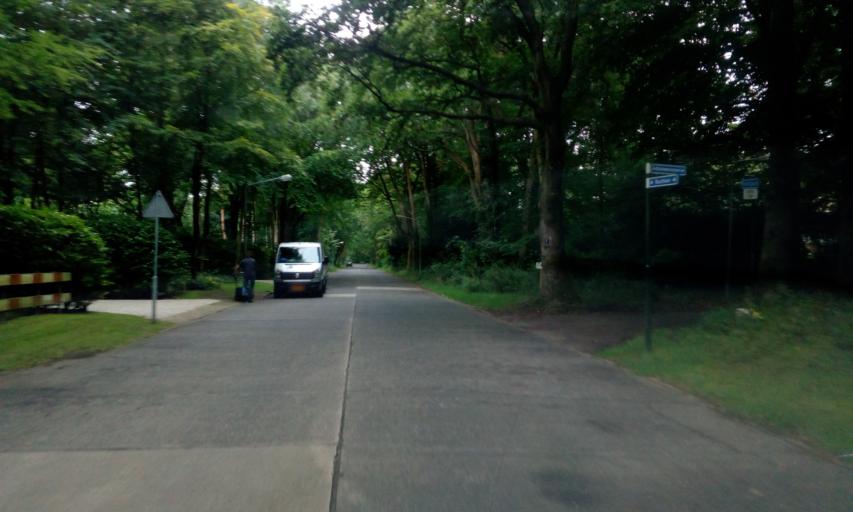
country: NL
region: North Holland
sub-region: Gemeente Hilversum
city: Hilversum
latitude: 52.2408
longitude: 5.1513
